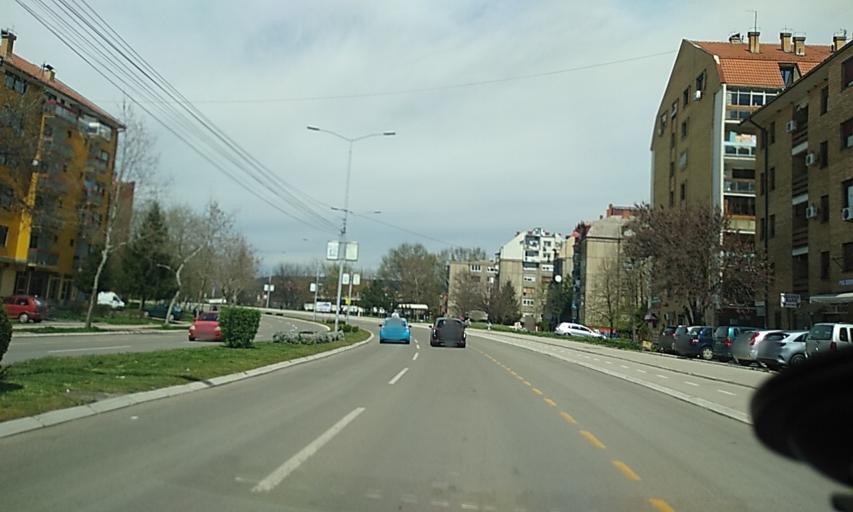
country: RS
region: Central Serbia
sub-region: Nisavski Okrug
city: Nis
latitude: 43.3143
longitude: 21.9276
